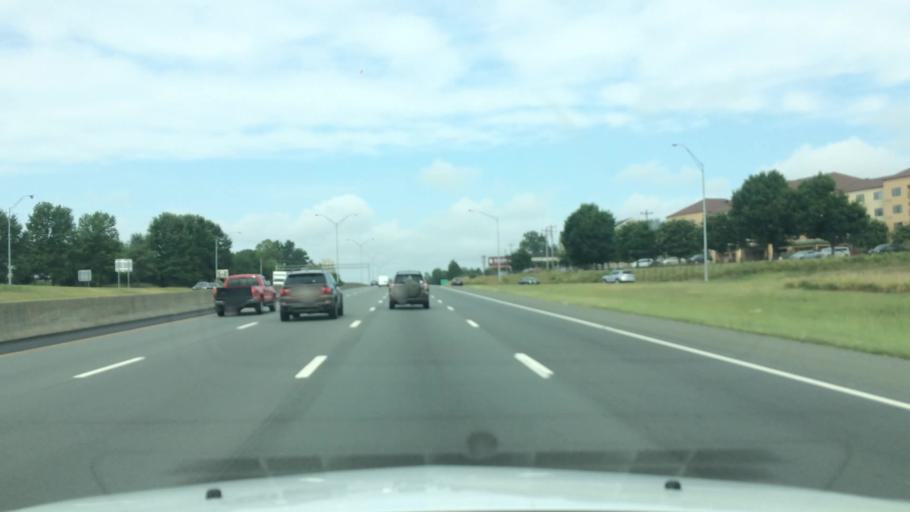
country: US
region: North Carolina
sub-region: Alamance County
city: Elon
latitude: 36.0676
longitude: -79.4991
